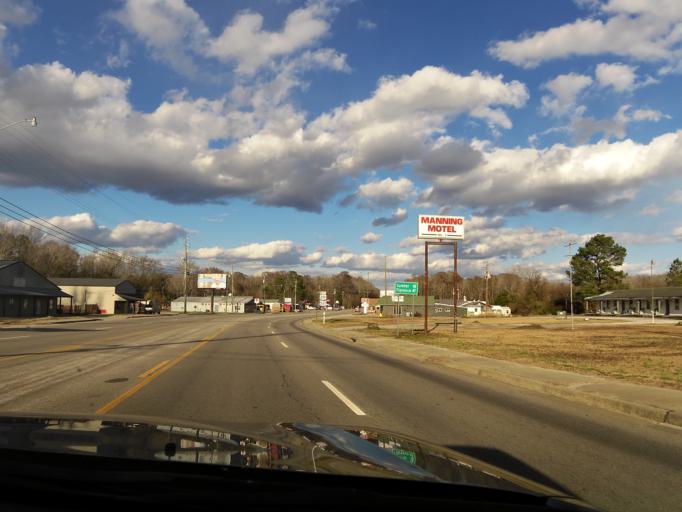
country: US
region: South Carolina
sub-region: Clarendon County
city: Manning
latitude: 33.7062
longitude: -80.2084
